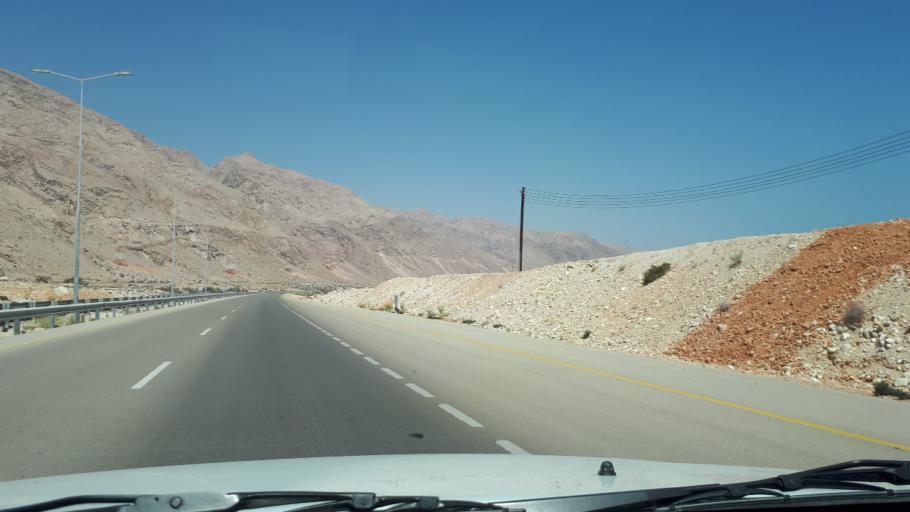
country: OM
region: Ash Sharqiyah
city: Sur
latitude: 22.7481
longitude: 59.3163
